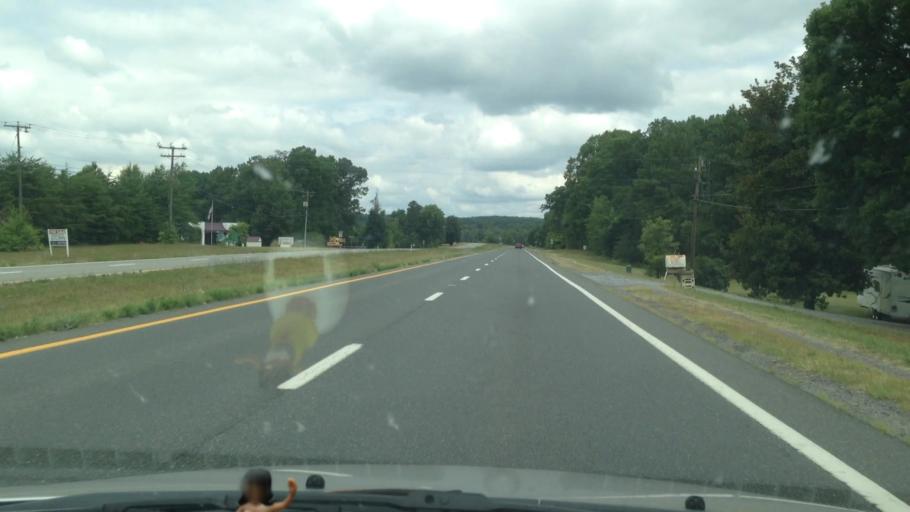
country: US
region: Virginia
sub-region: Campbell County
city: Rustburg
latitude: 37.2411
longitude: -79.1867
